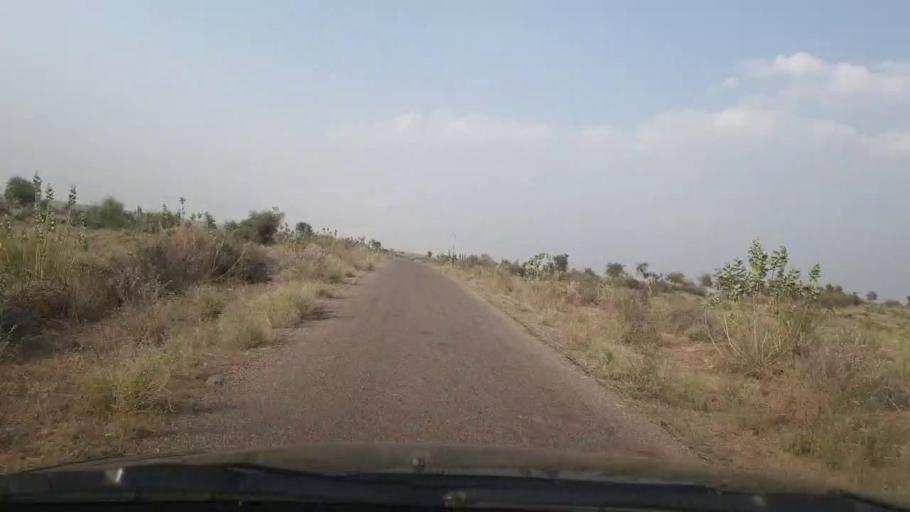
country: PK
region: Sindh
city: Islamkot
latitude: 25.0514
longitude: 70.5589
